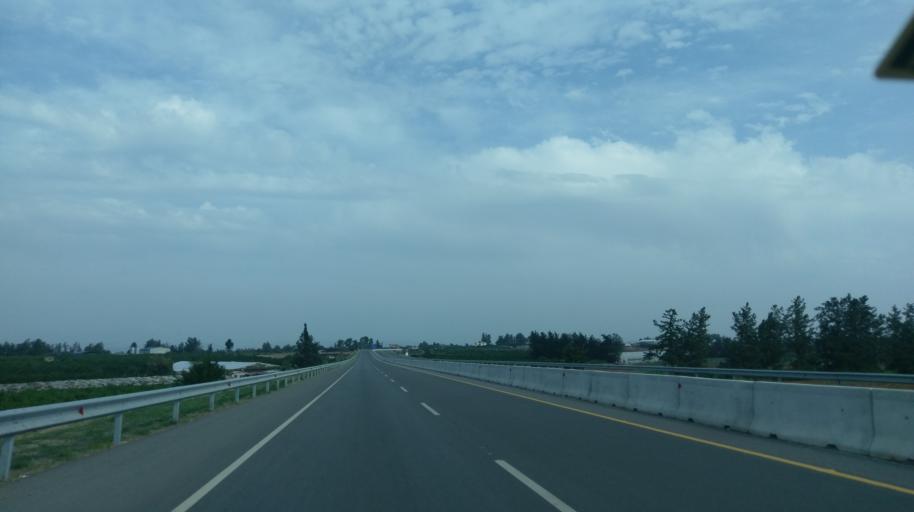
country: CY
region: Lefkosia
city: Morfou
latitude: 35.1703
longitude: 32.9472
